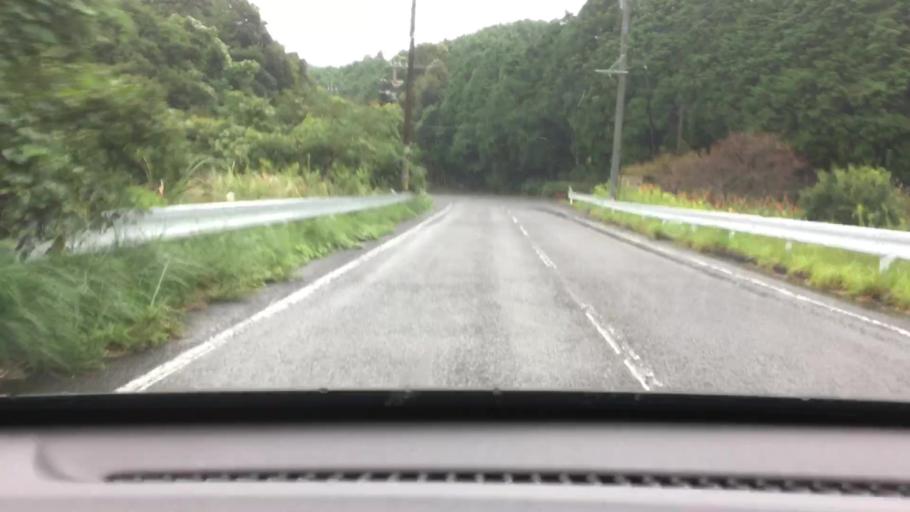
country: JP
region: Nagasaki
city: Togitsu
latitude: 32.8782
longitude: 129.7604
